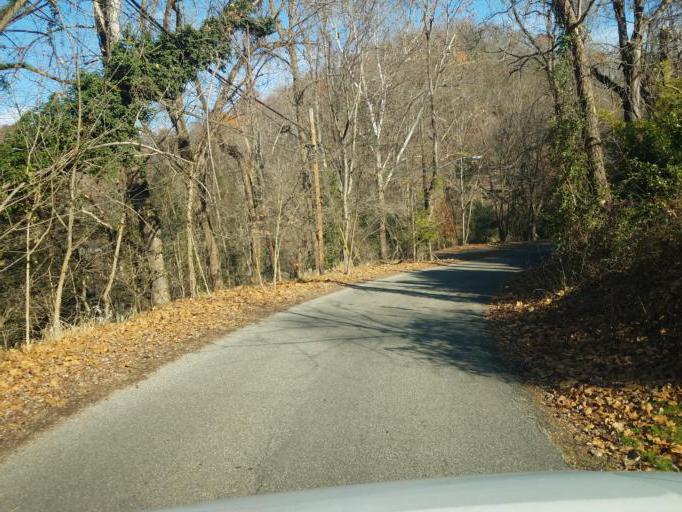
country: US
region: Ohio
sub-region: Scioto County
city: New Boston
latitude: 38.7543
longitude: -82.9632
